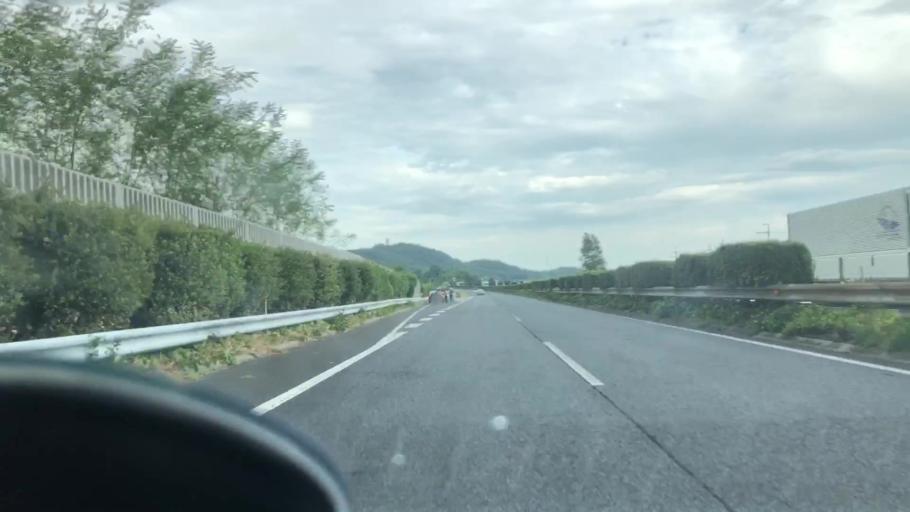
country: JP
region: Hyogo
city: Ono
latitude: 34.9367
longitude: 134.8340
